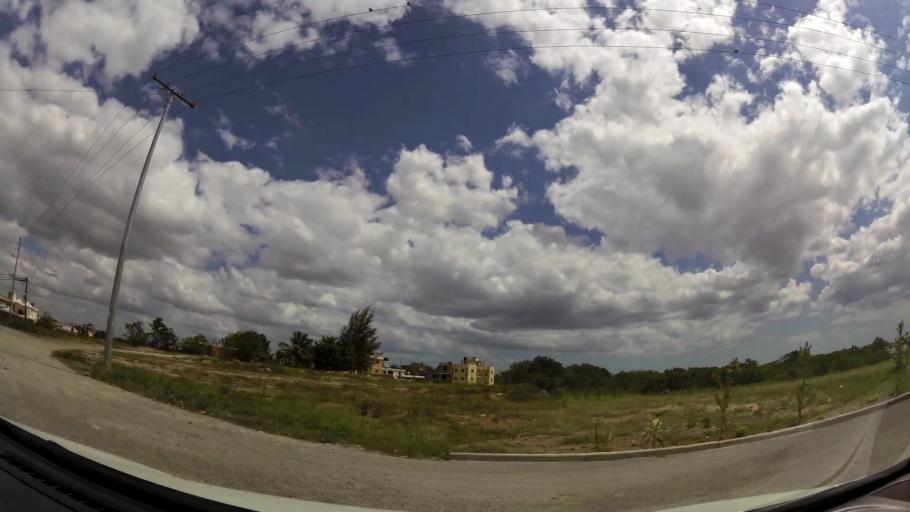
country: DO
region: Nacional
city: Ensanche Luperon
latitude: 18.5259
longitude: -69.8966
